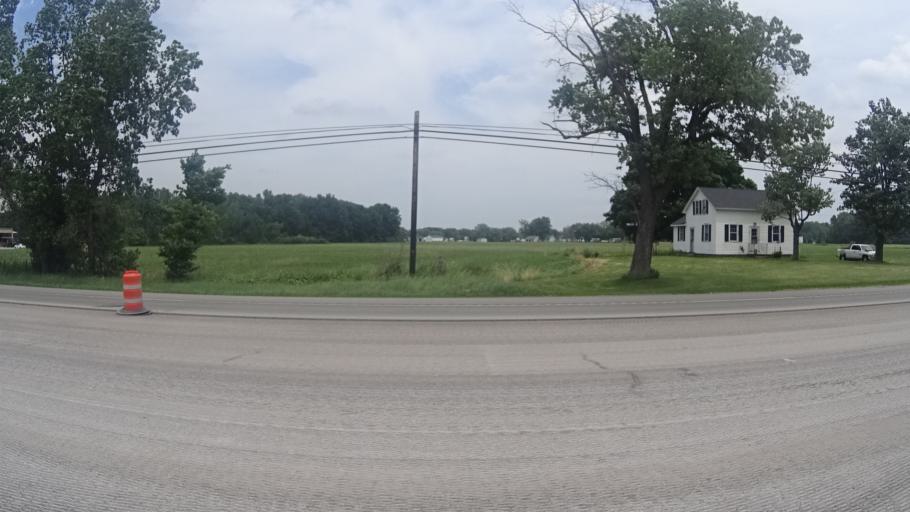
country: US
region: Ohio
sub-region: Erie County
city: Milan
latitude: 41.3136
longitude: -82.6087
